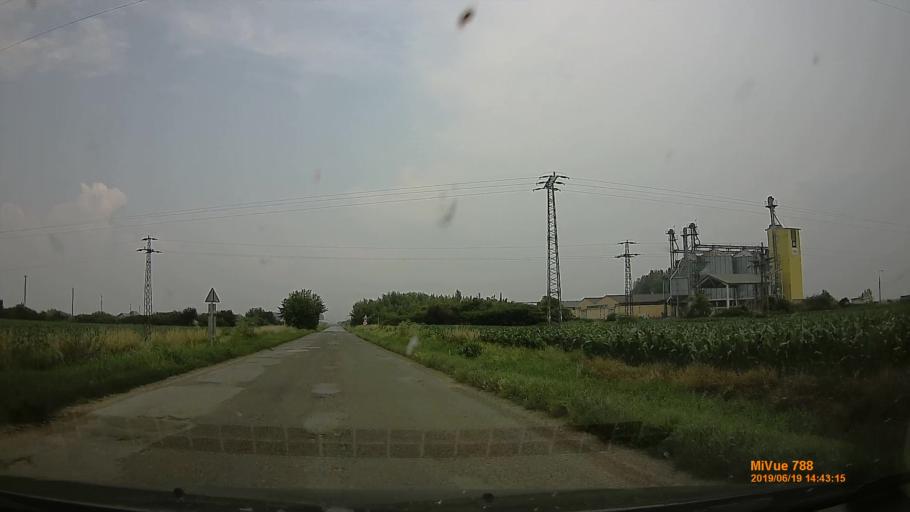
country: HU
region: Baranya
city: Szigetvar
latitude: 46.0410
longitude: 17.8179
